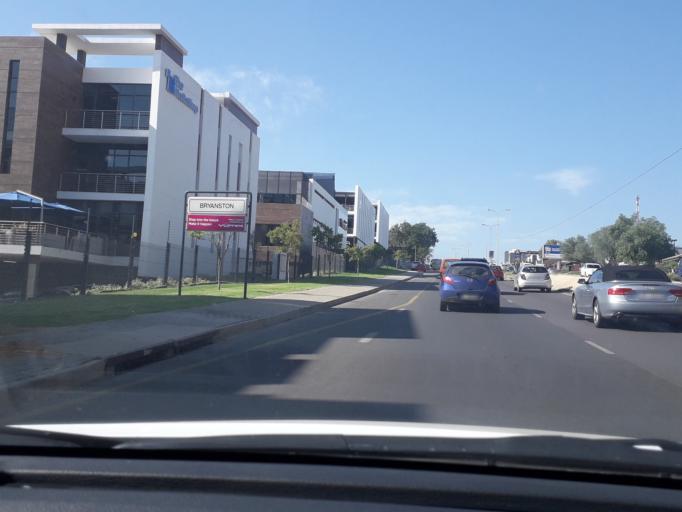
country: ZA
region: Gauteng
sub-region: City of Johannesburg Metropolitan Municipality
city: Diepsloot
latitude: -26.0505
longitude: 28.0243
